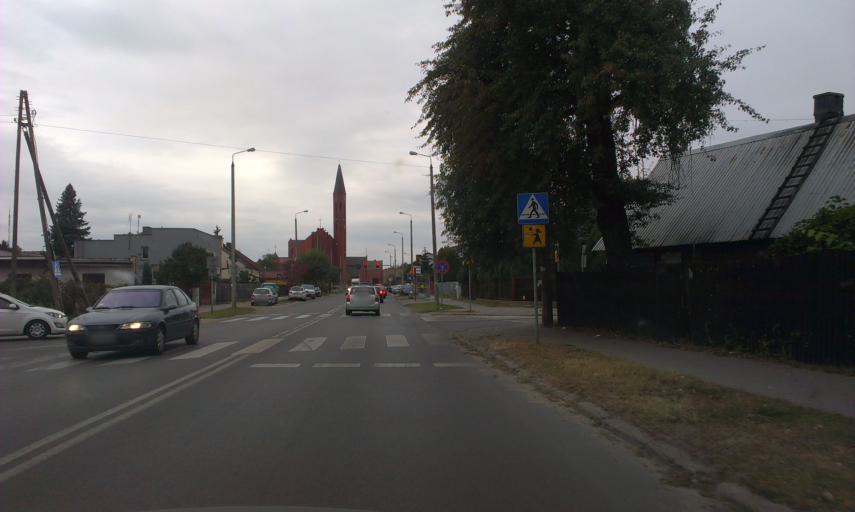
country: PL
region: Masovian Voivodeship
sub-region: Radom
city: Radom
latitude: 51.4104
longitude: 21.1364
